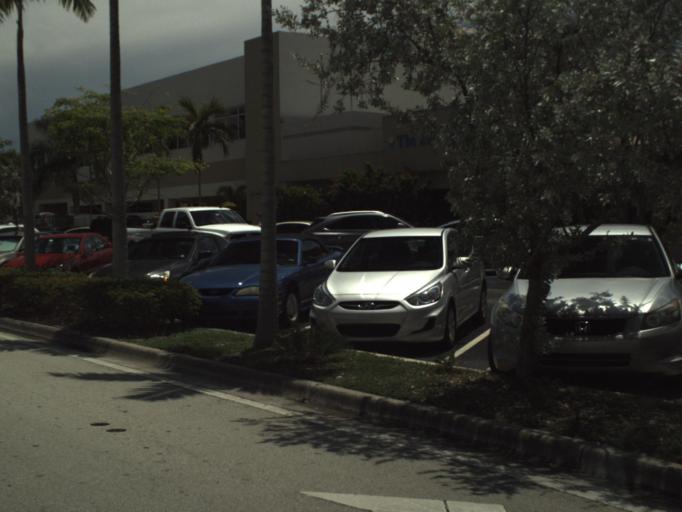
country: US
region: Florida
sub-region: Broward County
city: Lauderdale-by-the-Sea
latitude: 26.1898
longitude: -80.1052
